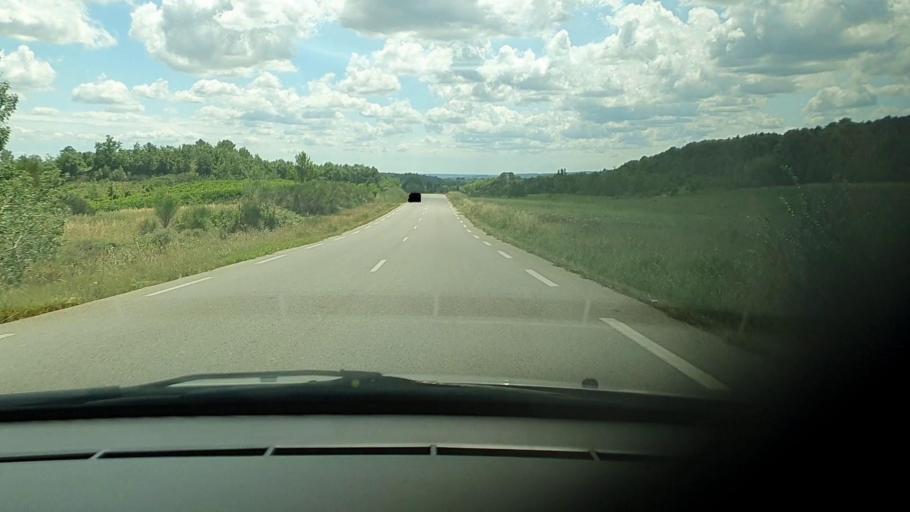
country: FR
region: Languedoc-Roussillon
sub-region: Departement du Gard
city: Moussac
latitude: 44.0420
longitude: 4.2326
